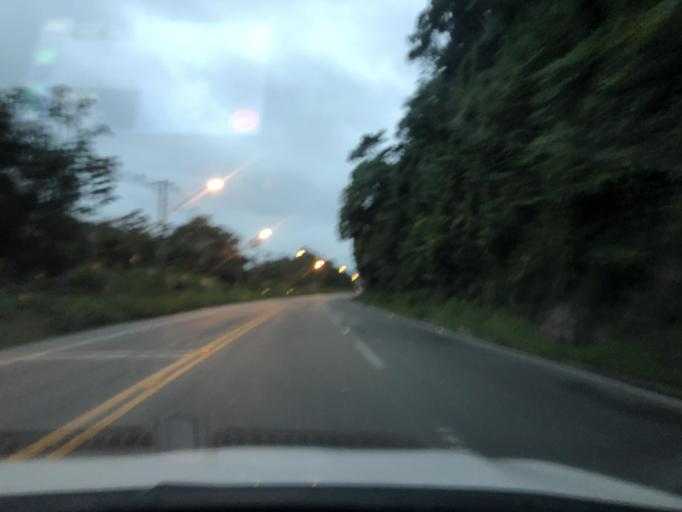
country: BR
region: Santa Catarina
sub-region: Pomerode
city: Pomerode
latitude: -26.7462
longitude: -49.0698
